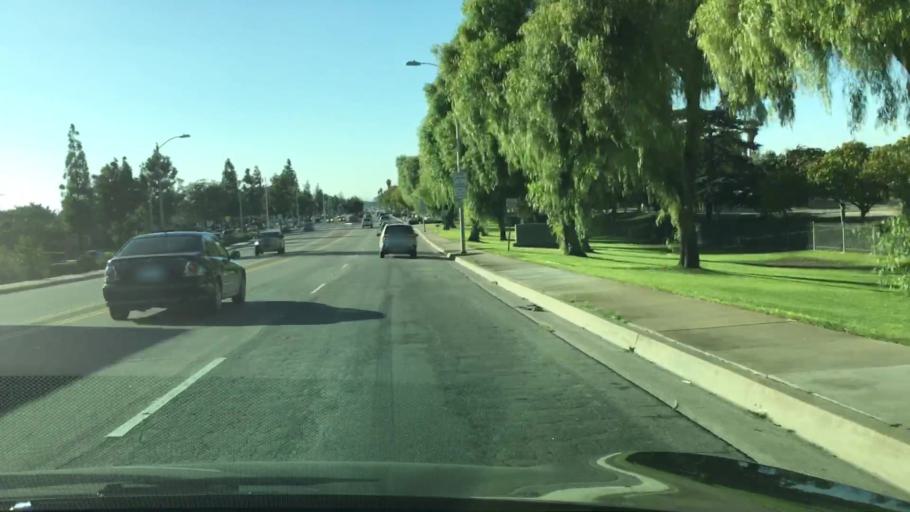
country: US
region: California
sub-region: Los Angeles County
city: Pico Rivera
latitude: 33.9761
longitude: -118.0841
